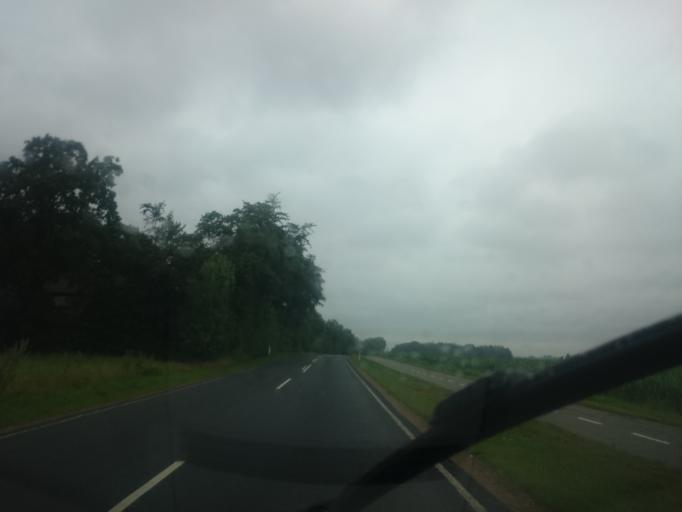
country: DK
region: South Denmark
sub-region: Vejen Kommune
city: Holsted
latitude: 55.6128
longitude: 8.8027
